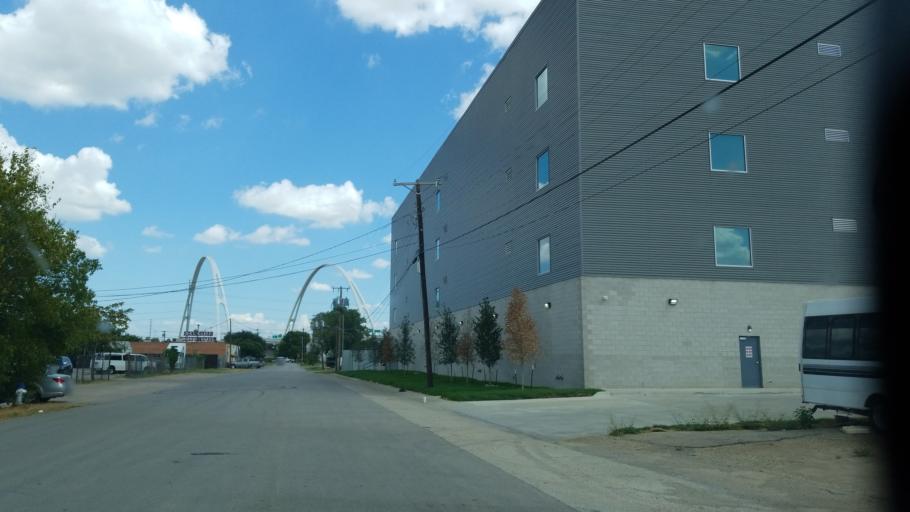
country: US
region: Texas
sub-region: Dallas County
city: Dallas
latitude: 32.7700
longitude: -96.8261
